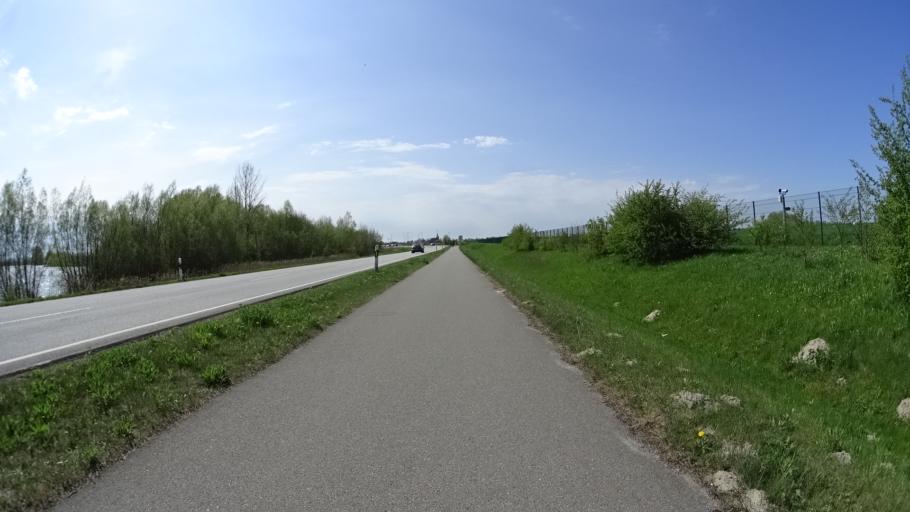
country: DE
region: Lower Saxony
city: Neu Wulmstorf
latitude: 53.5286
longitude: 9.8258
